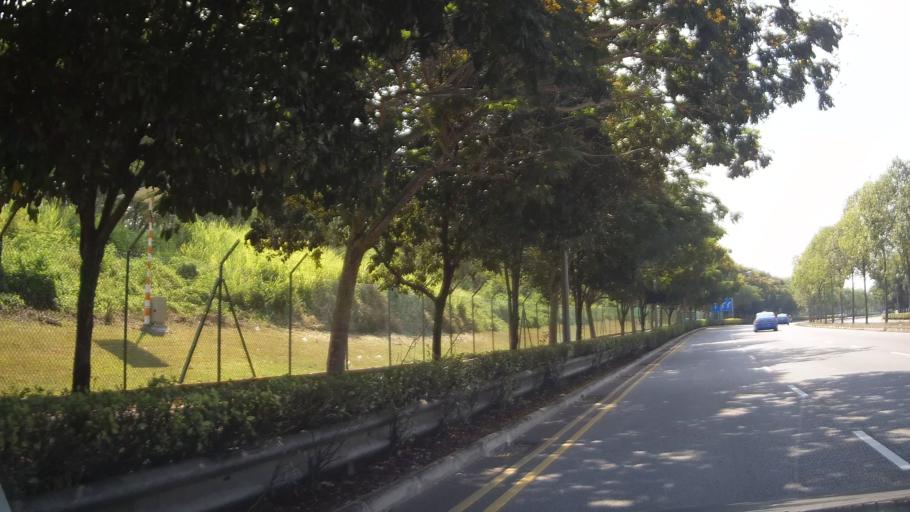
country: MY
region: Johor
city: Kampung Pasir Gudang Baru
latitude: 1.3793
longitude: 103.9073
